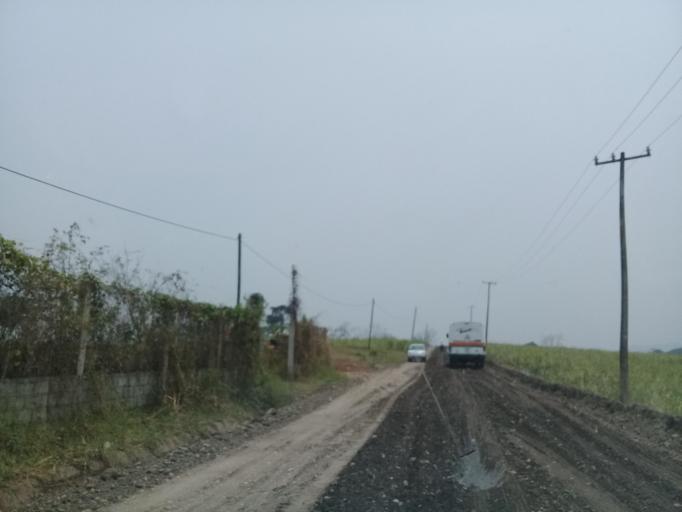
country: MX
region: Veracruz
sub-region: Tezonapa
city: Laguna Chica (Pueblo Nuevo)
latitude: 18.5411
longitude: -96.7385
